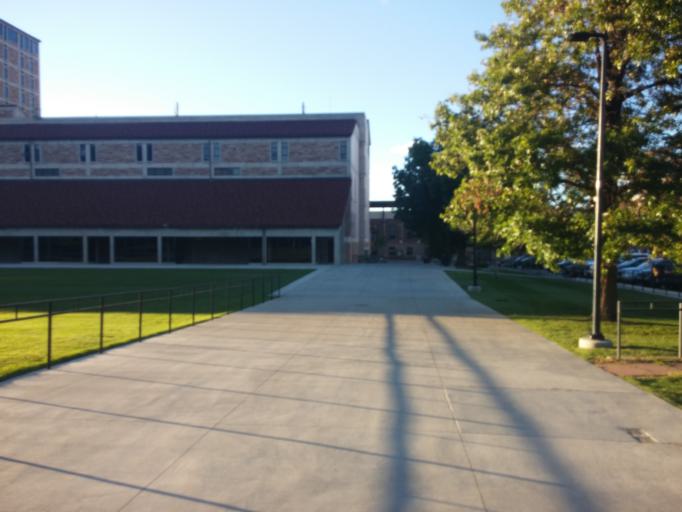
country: US
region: Colorado
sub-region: Boulder County
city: Boulder
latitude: 40.0074
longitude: -105.2670
